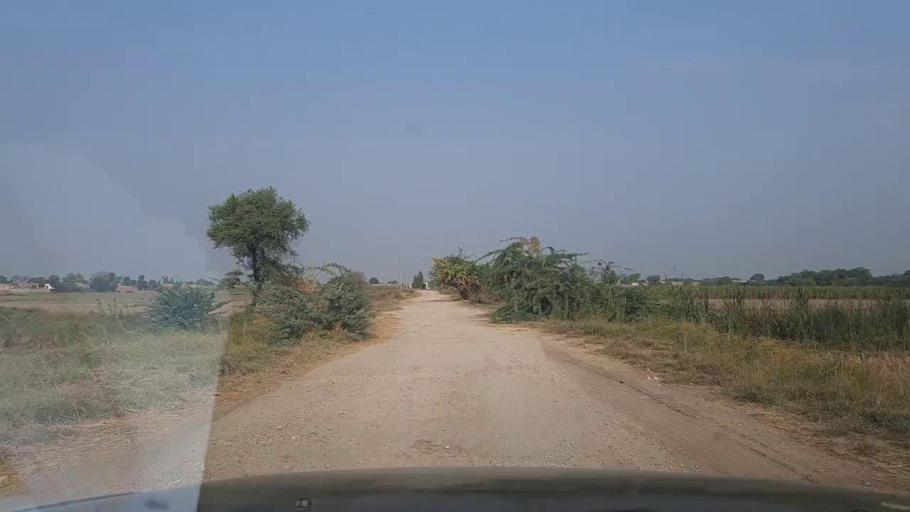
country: PK
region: Sindh
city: Bulri
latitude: 24.9382
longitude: 68.2822
